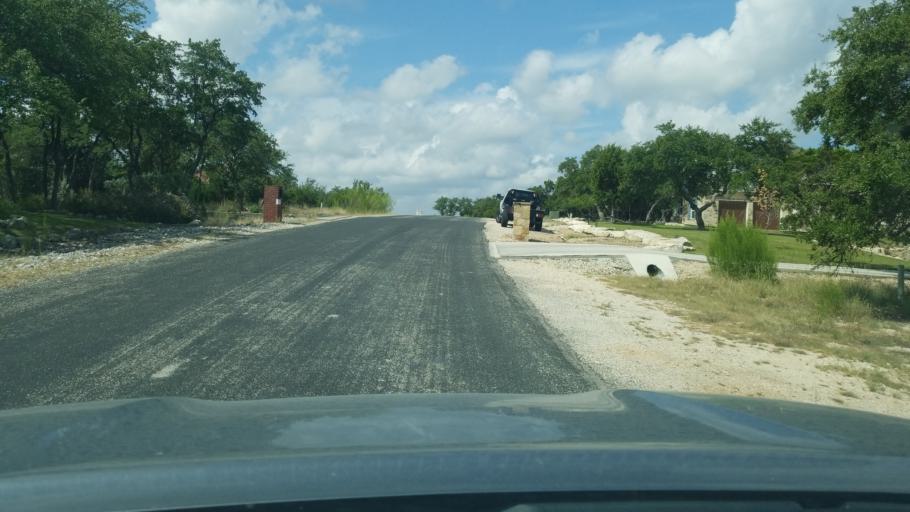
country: US
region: Texas
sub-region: Bexar County
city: Timberwood Park
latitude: 29.6869
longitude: -98.5156
